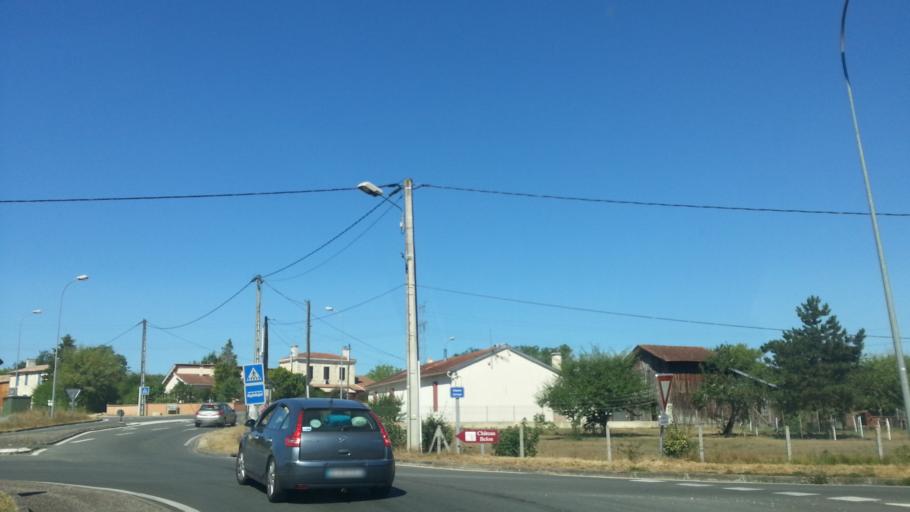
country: FR
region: Aquitaine
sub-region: Departement de la Gironde
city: Saint-Selve
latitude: 44.6736
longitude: -0.4933
